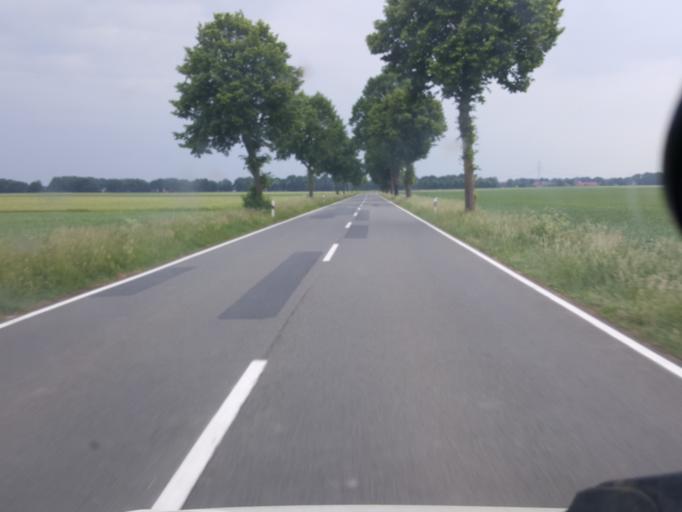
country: DE
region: Lower Saxony
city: Raddestorf
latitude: 52.4728
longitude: 8.9857
